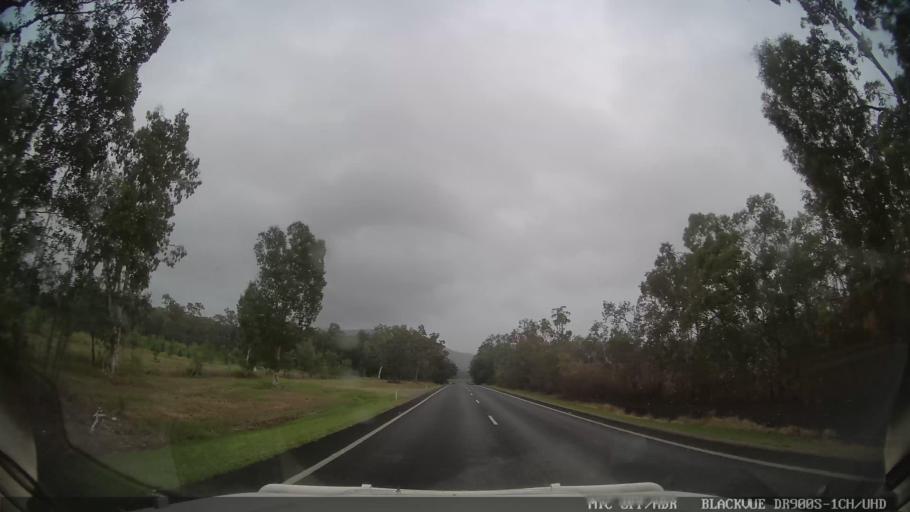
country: AU
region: Queensland
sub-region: Hinchinbrook
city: Ingham
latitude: -18.4434
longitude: 146.1404
